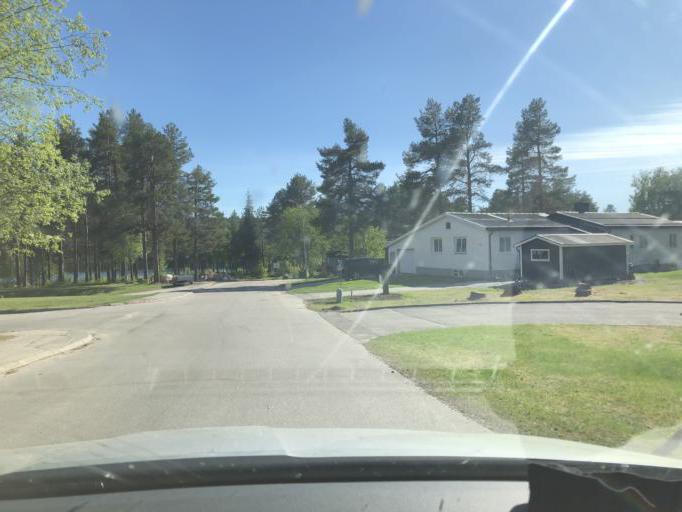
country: SE
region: Norrbotten
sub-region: Jokkmokks Kommun
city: Jokkmokk
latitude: 66.6032
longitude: 19.8290
